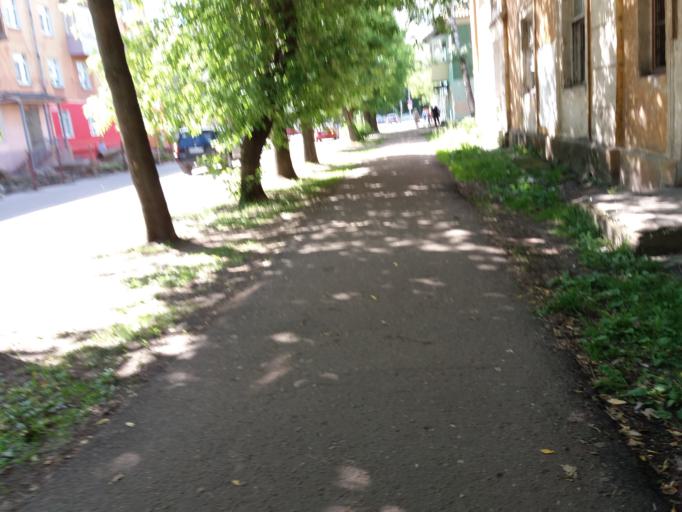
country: RU
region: Jaroslavl
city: Yaroslavl
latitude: 57.6384
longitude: 39.8396
